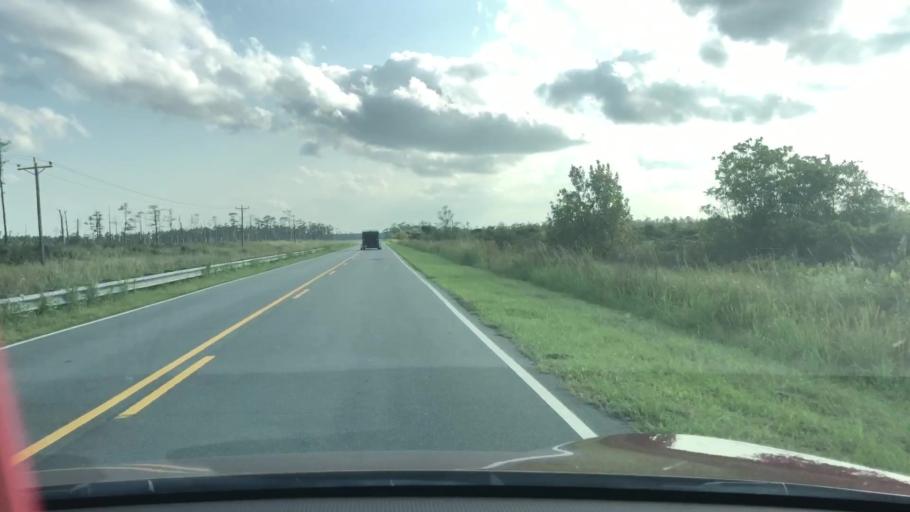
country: US
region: North Carolina
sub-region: Dare County
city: Wanchese
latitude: 35.6214
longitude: -75.7878
